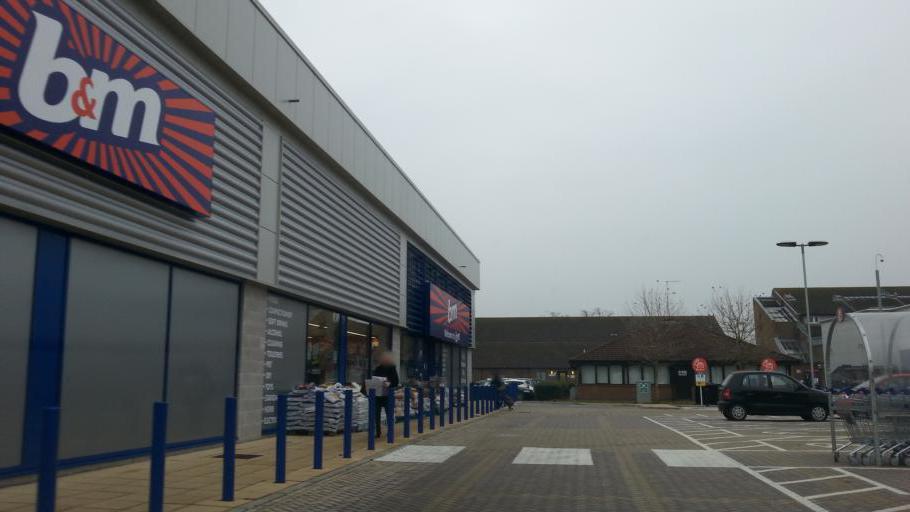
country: GB
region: England
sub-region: Peterborough
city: Castor
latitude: 52.5440
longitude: -0.3041
